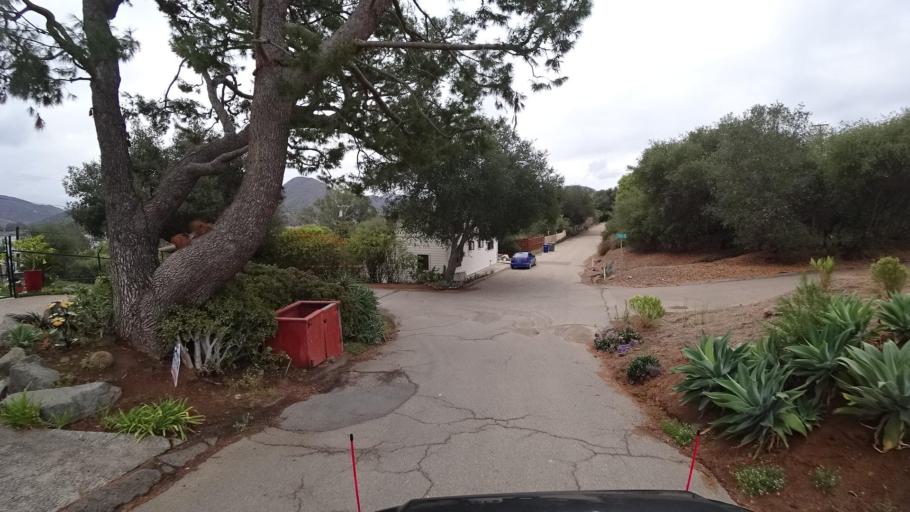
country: US
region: California
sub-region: San Diego County
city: Escondido
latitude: 33.0708
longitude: -117.1193
